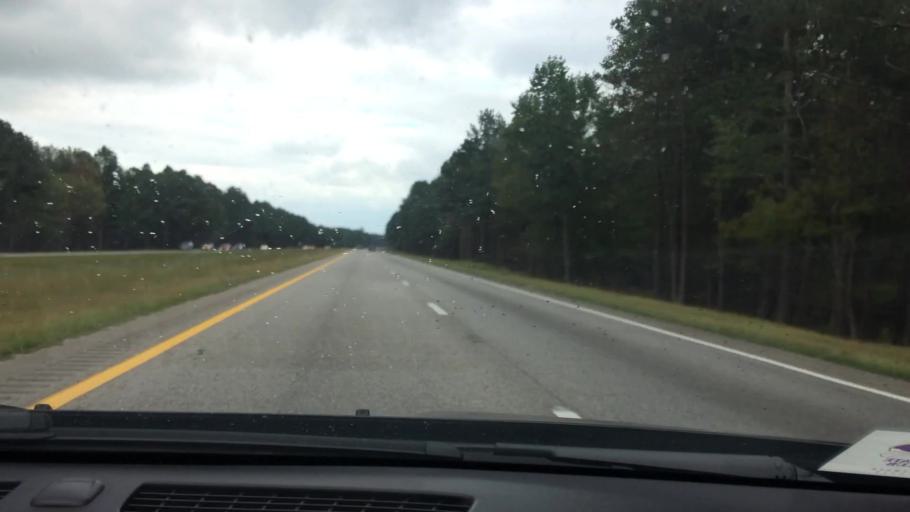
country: US
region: North Carolina
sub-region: Wake County
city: Zebulon
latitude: 35.8083
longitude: -78.2179
